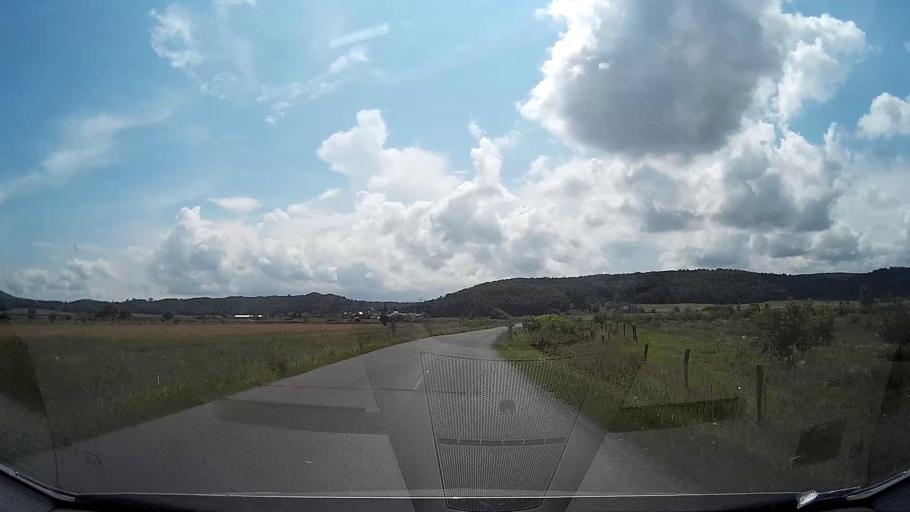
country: SK
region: Banskobystricky
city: Fil'akovo
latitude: 48.2947
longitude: 19.7904
